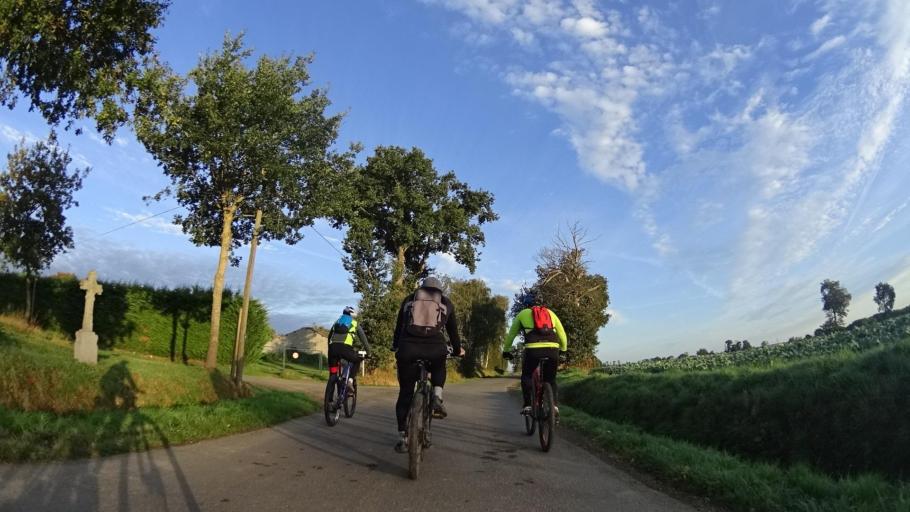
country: FR
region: Brittany
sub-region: Departement des Cotes-d'Armor
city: Evran
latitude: 48.3542
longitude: -1.9429
